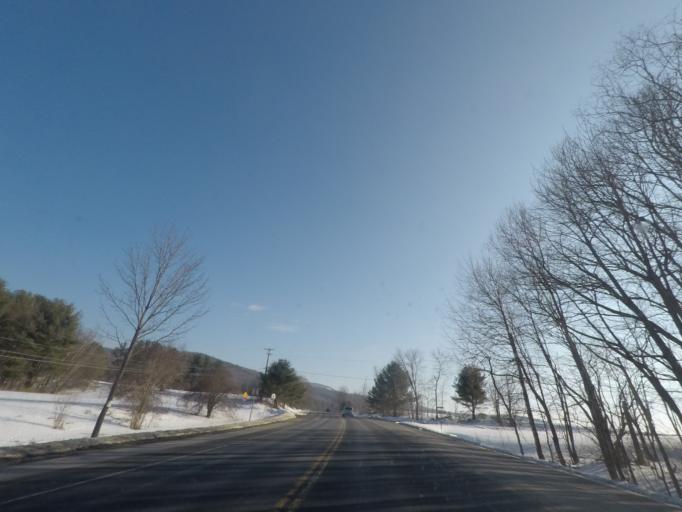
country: US
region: Massachusetts
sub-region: Berkshire County
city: Lanesborough
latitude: 42.5327
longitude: -73.3583
